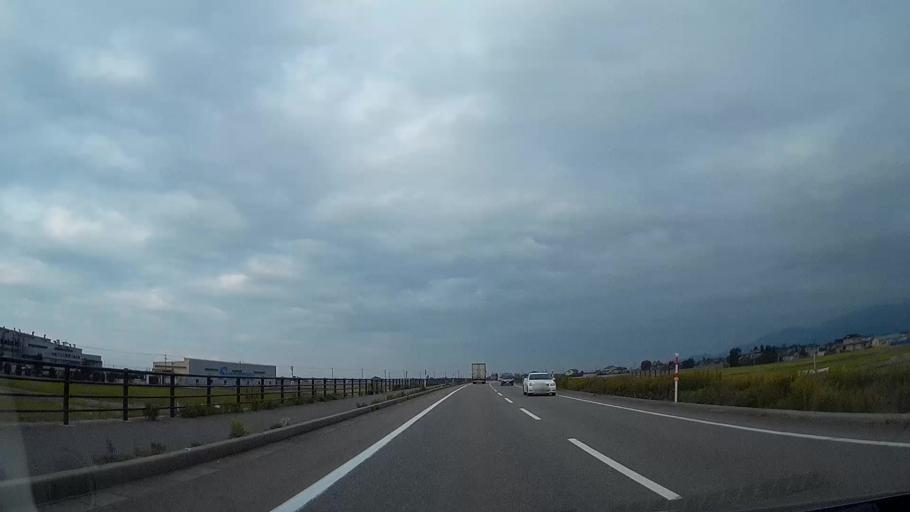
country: JP
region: Toyama
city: Nyuzen
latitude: 36.9235
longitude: 137.4697
